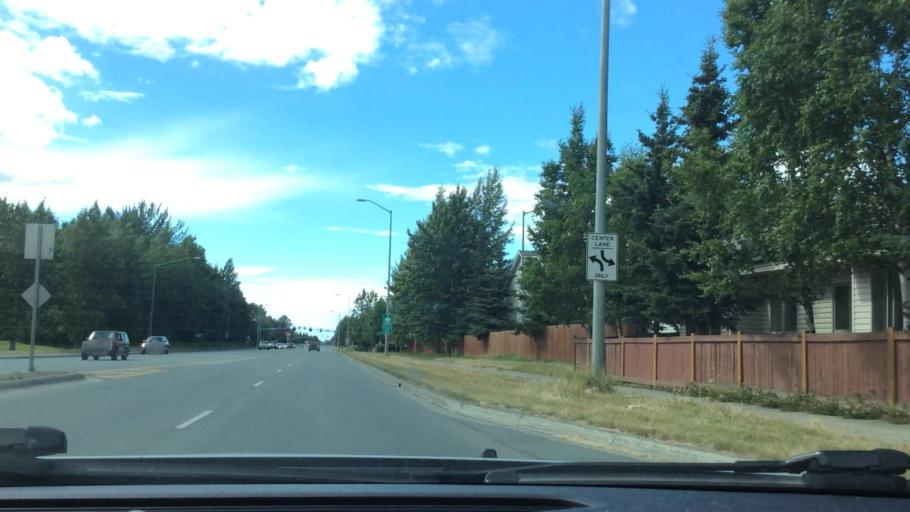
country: US
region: Alaska
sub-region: Anchorage Municipality
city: Anchorage
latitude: 61.2098
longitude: -149.7947
